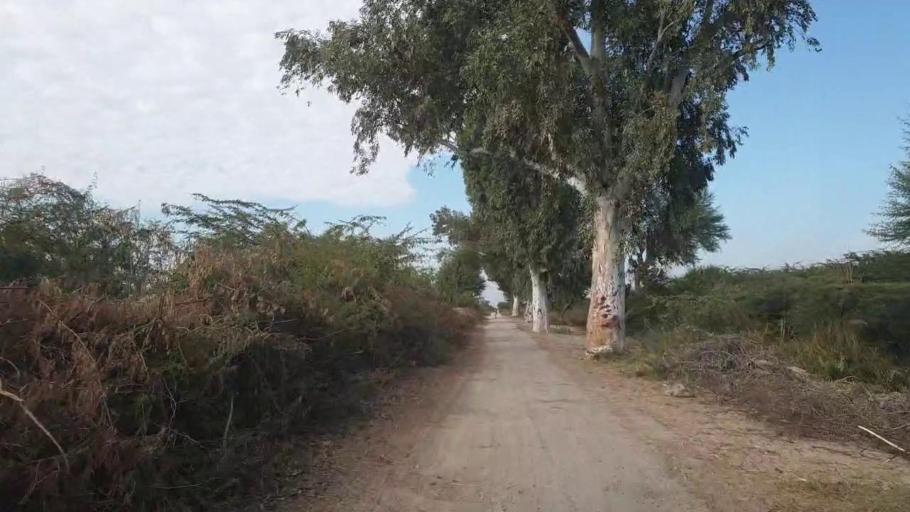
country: PK
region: Sindh
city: Sinjhoro
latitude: 26.0473
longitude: 68.8762
